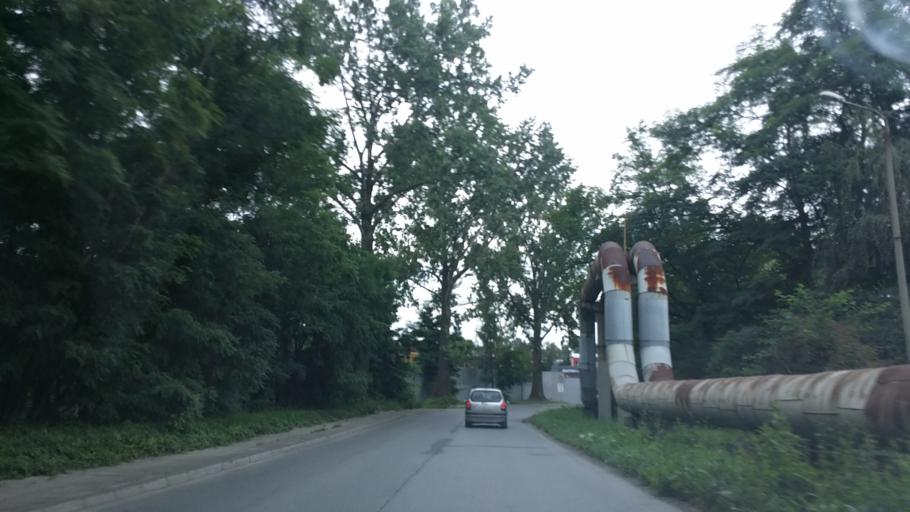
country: PL
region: Lesser Poland Voivodeship
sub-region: Powiat krakowski
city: Skawina
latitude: 49.9764
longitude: 19.8090
